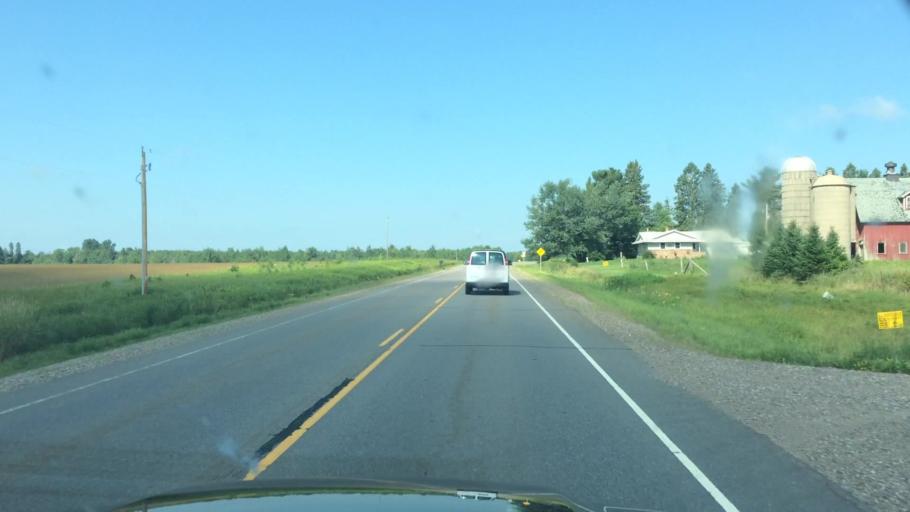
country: US
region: Wisconsin
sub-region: Lincoln County
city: Merrill
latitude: 45.1484
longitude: -89.4594
